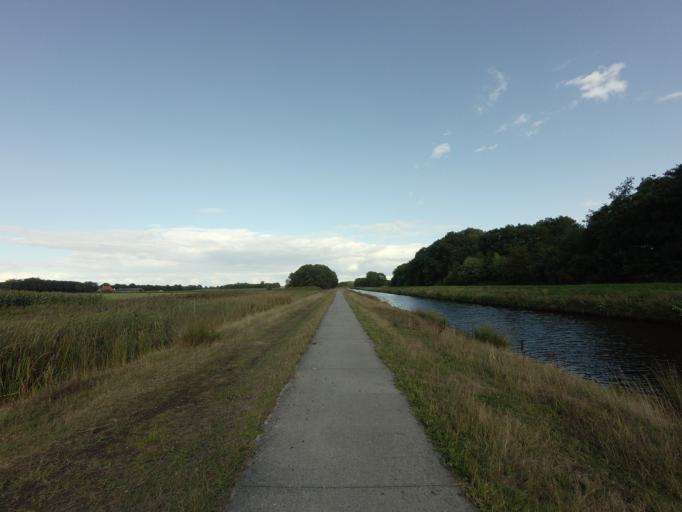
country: NL
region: Friesland
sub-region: Gemeente Heerenveen
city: Jubbega
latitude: 52.9949
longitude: 6.2190
